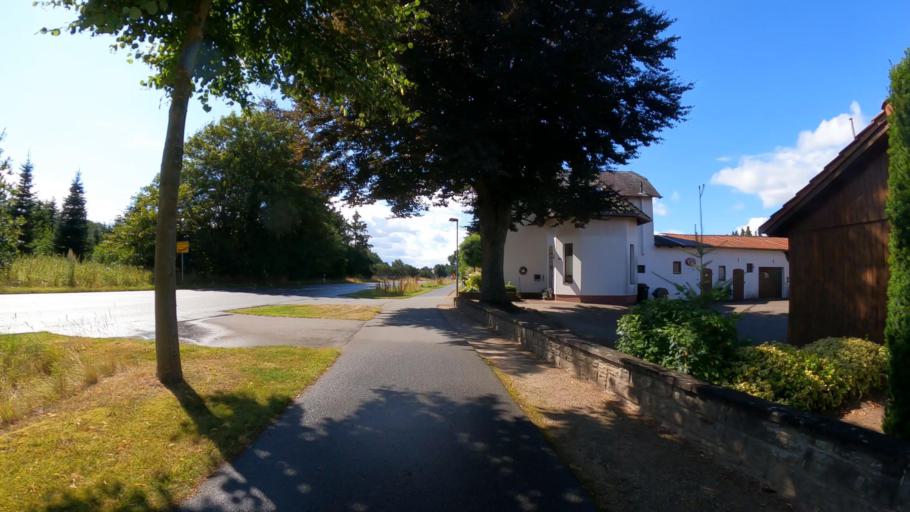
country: DE
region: Schleswig-Holstein
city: Wiemersdorf
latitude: 53.9474
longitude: 9.8982
